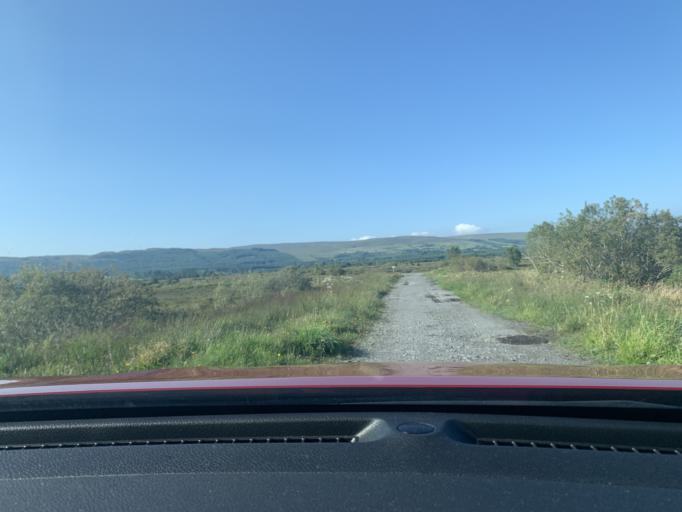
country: IE
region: Connaught
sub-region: Sligo
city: Tobercurry
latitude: 54.0694
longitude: -8.7996
